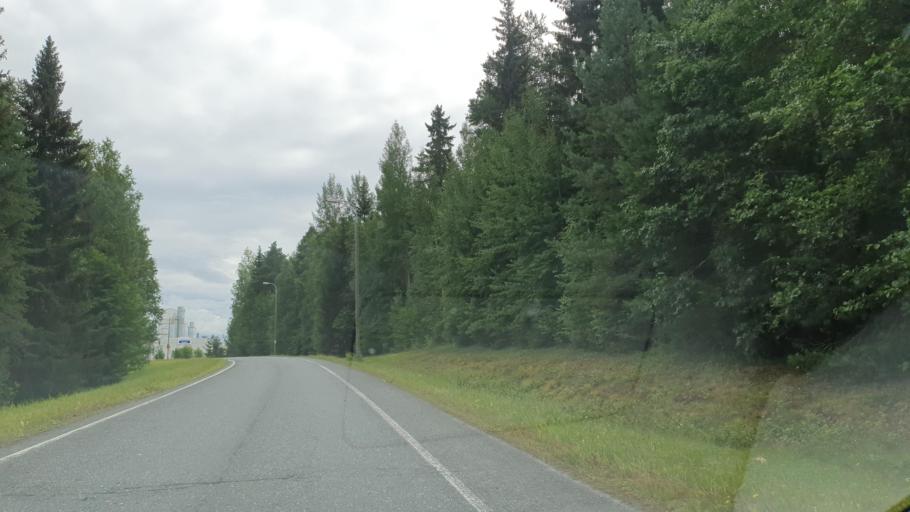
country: FI
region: Northern Savo
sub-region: Ylae-Savo
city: Iisalmi
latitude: 63.5260
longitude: 27.2460
